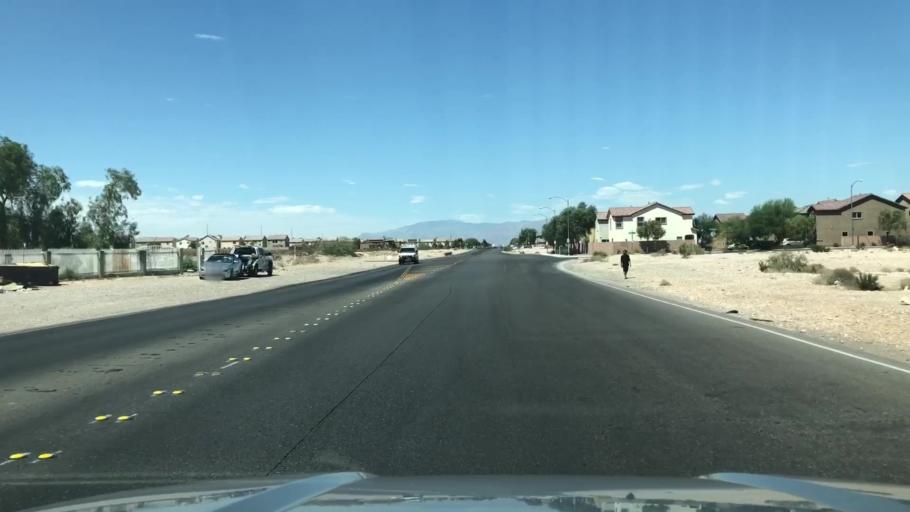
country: US
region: Nevada
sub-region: Clark County
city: Enterprise
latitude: 36.0378
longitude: -115.2078
